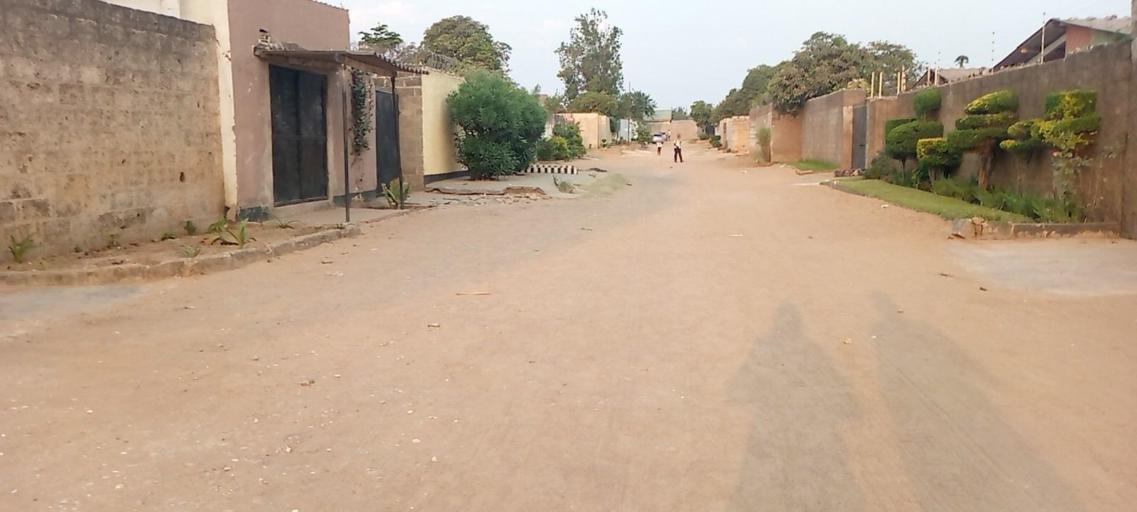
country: ZM
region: Lusaka
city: Lusaka
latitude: -15.4057
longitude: 28.3471
